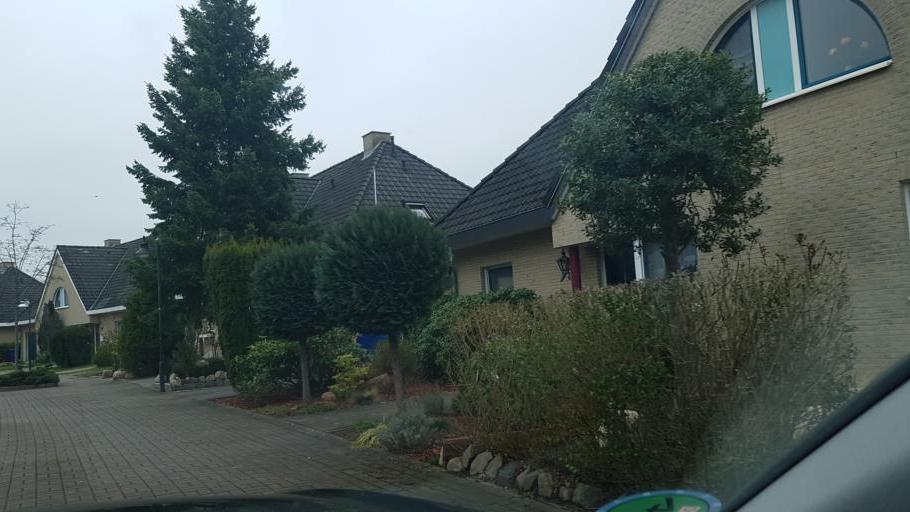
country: DE
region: Brandenburg
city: Mittenwalde
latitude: 52.2851
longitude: 13.5395
